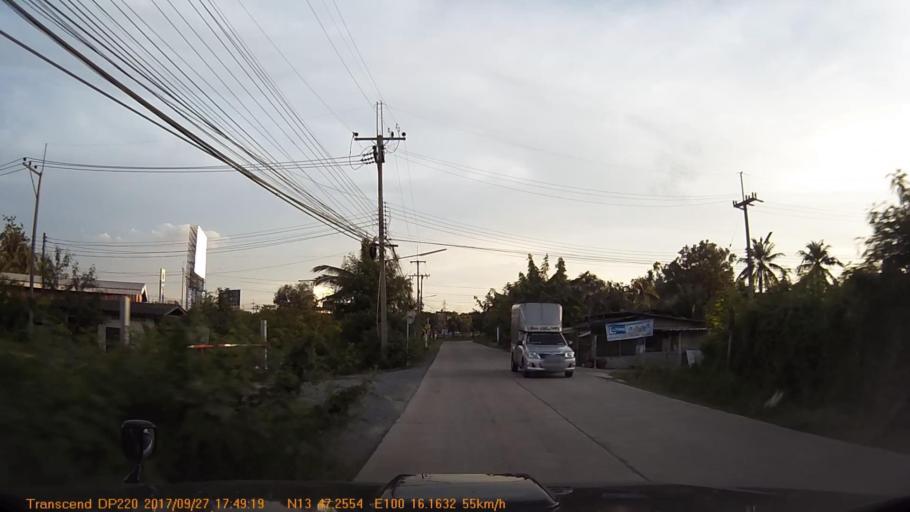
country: TH
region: Nakhon Pathom
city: Salaya
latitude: 13.7874
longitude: 100.2693
